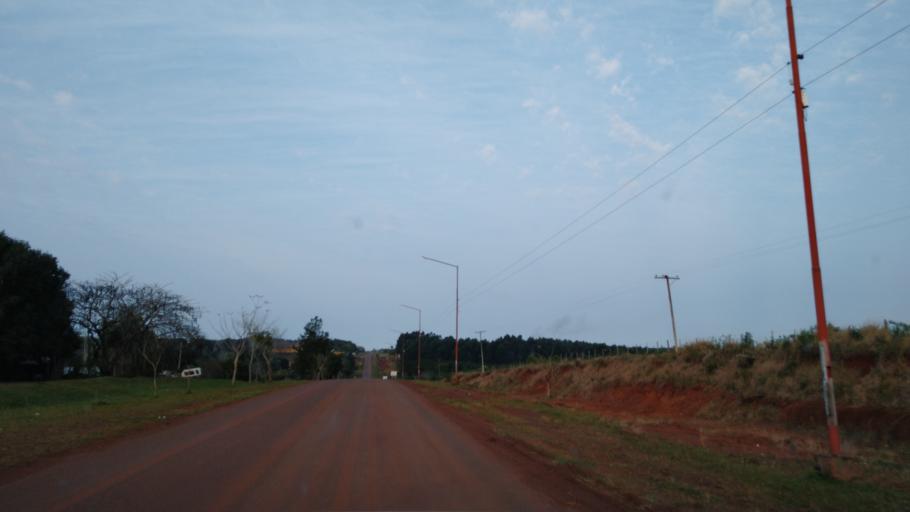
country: AR
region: Corrientes
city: San Carlos
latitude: -27.7519
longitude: -55.8954
